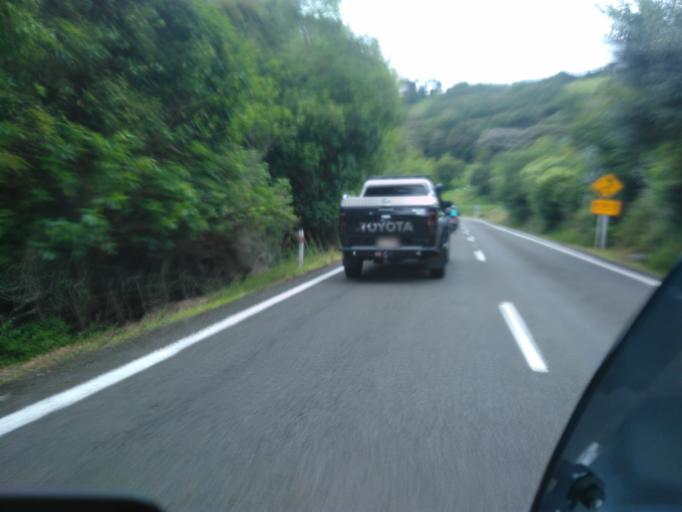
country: NZ
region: Gisborne
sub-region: Gisborne District
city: Gisborne
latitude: -38.4741
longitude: 177.6767
